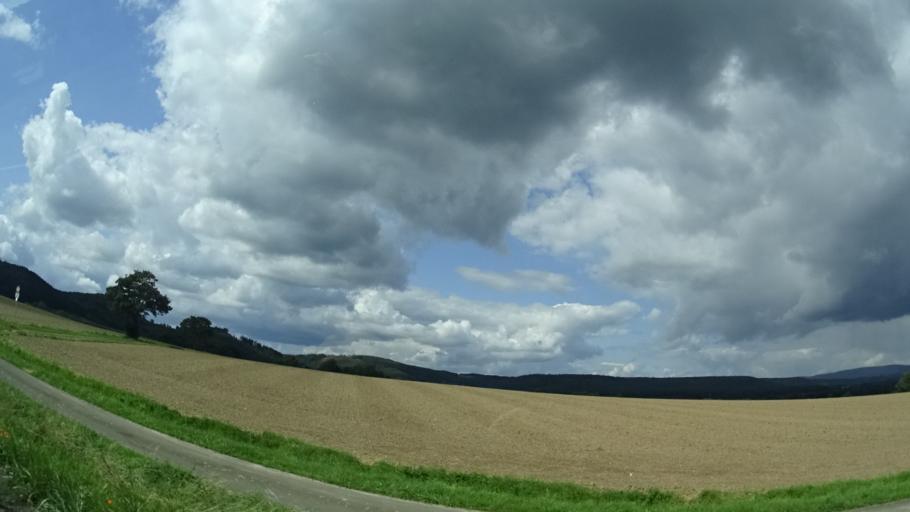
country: DE
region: Bavaria
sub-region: Upper Franconia
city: Neustadt bei Coburg
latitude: 50.2973
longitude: 11.0994
